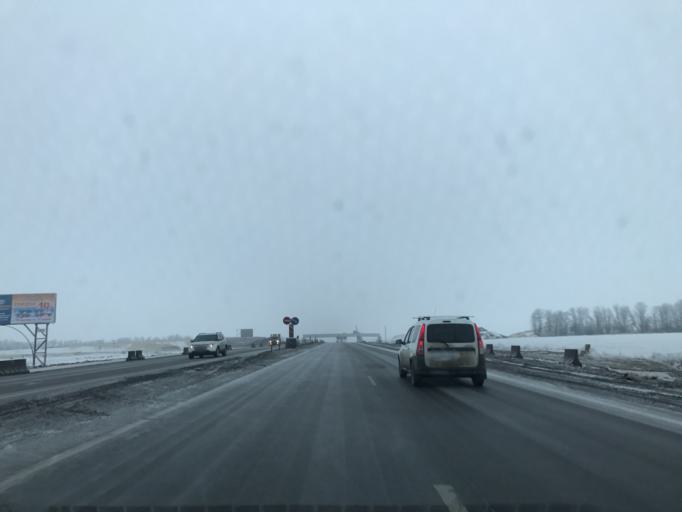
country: RU
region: Rostov
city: Grushevskaya
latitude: 47.4985
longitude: 39.9707
